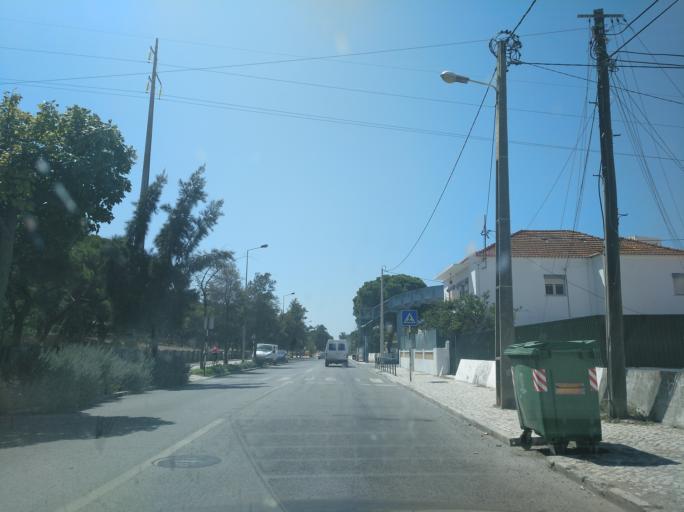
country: PT
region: Setubal
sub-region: Almada
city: Trafaria
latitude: 38.6703
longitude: -9.2375
